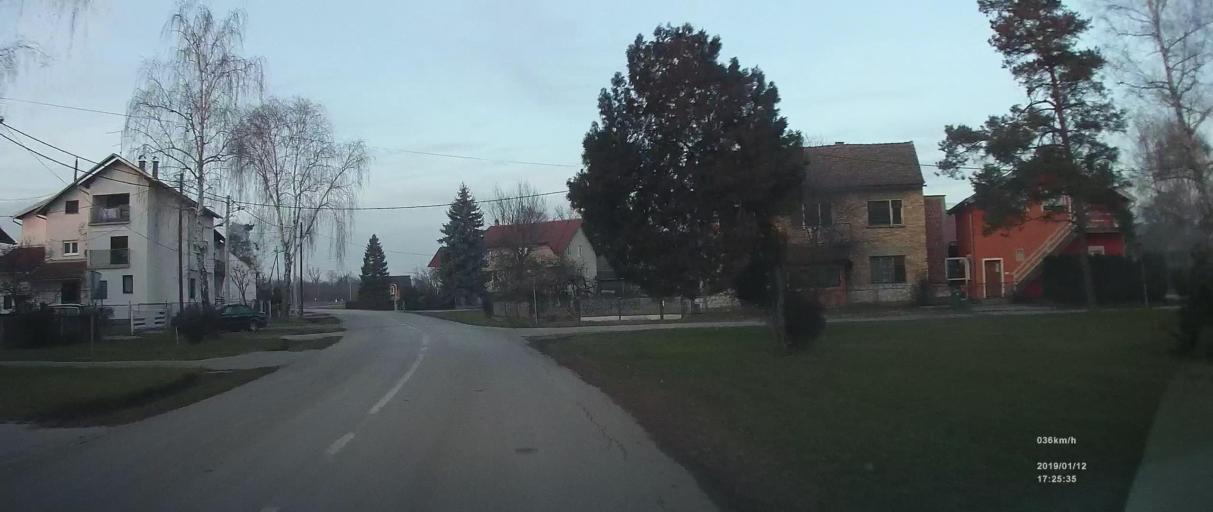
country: HR
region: Zagrebacka
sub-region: Grad Velika Gorica
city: Velika Gorica
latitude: 45.7323
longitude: 16.1014
